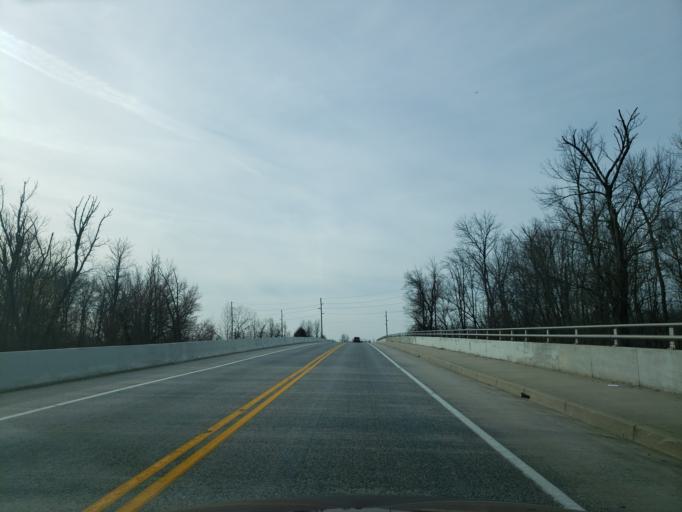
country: US
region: Delaware
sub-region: Kent County
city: Cheswold
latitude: 39.1912
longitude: -75.5589
